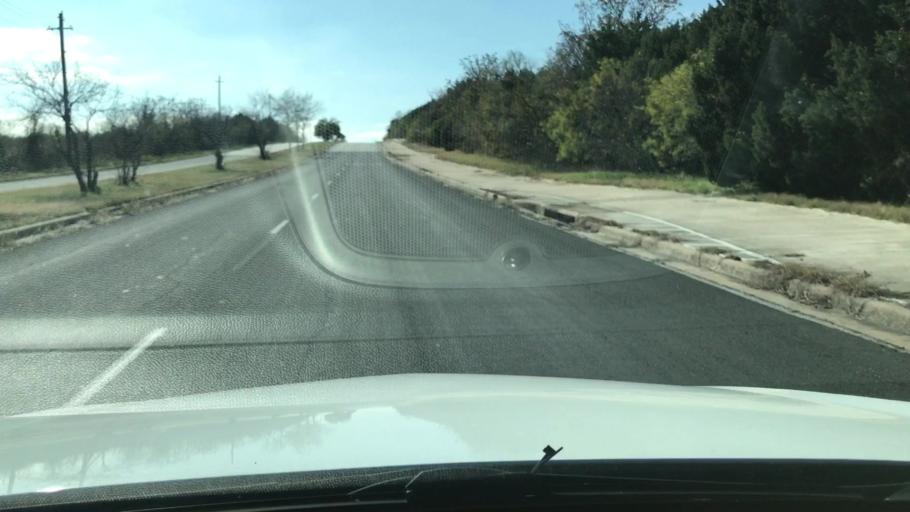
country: US
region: Texas
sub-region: Travis County
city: Onion Creek
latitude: 30.1768
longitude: -97.7216
